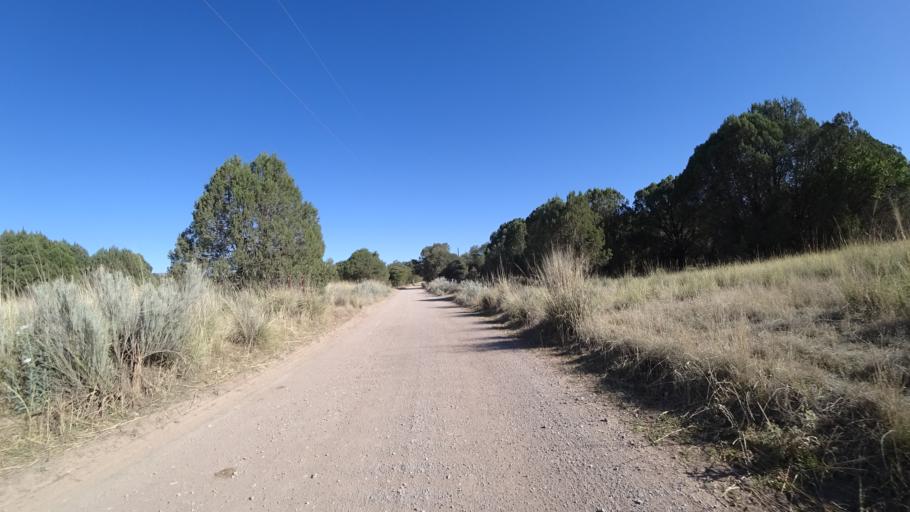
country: US
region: Arizona
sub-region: Cochise County
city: Huachuca City
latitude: 31.5377
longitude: -110.5299
